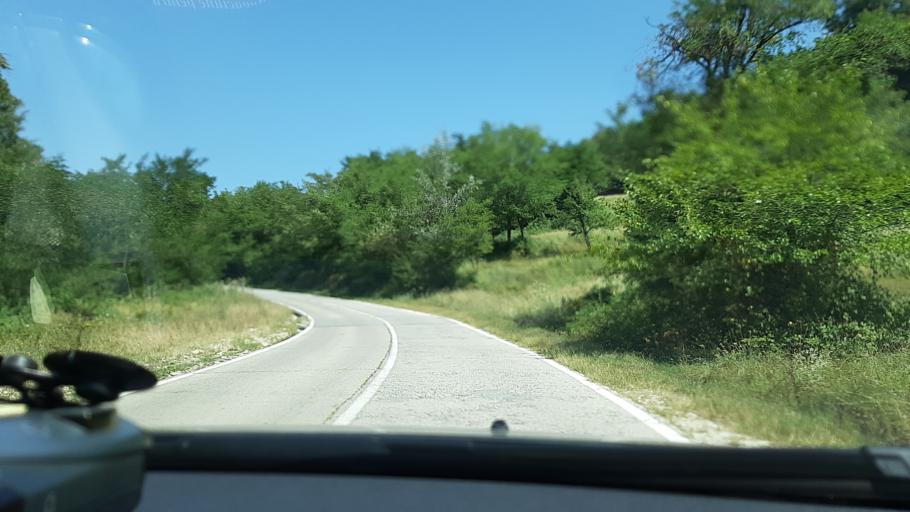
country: RO
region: Gorj
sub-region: Comuna Logresti-Mosteni
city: Logresti Mosteni
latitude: 44.9131
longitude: 23.7664
